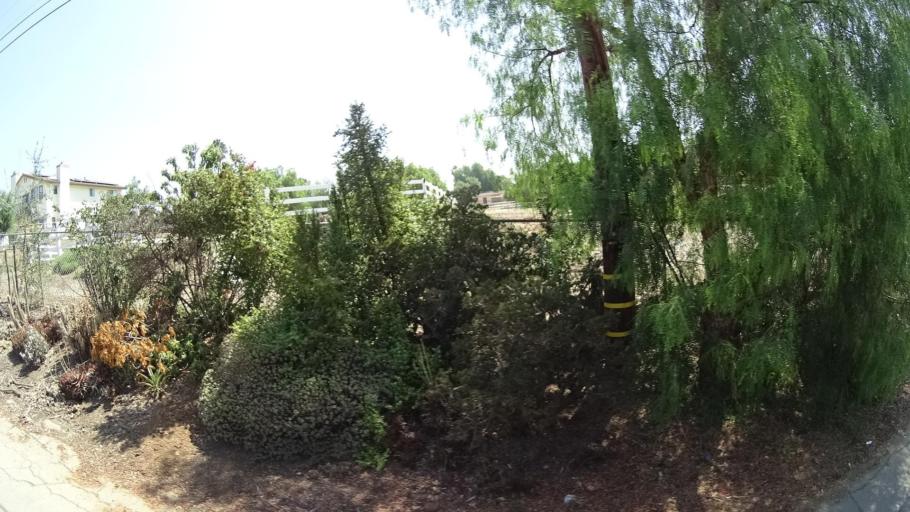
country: US
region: California
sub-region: San Diego County
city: Bonsall
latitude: 33.2477
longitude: -117.2327
